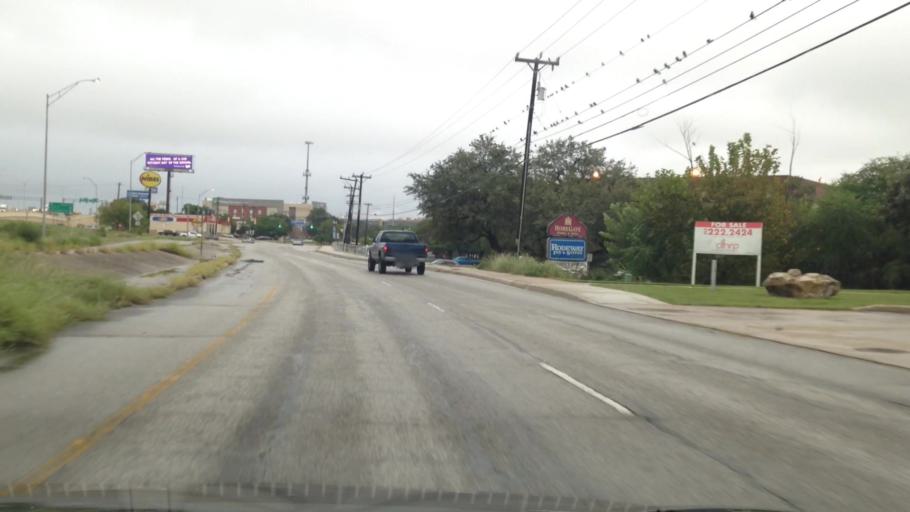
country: US
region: Texas
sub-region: Bexar County
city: Shavano Park
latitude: 29.5479
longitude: -98.5851
